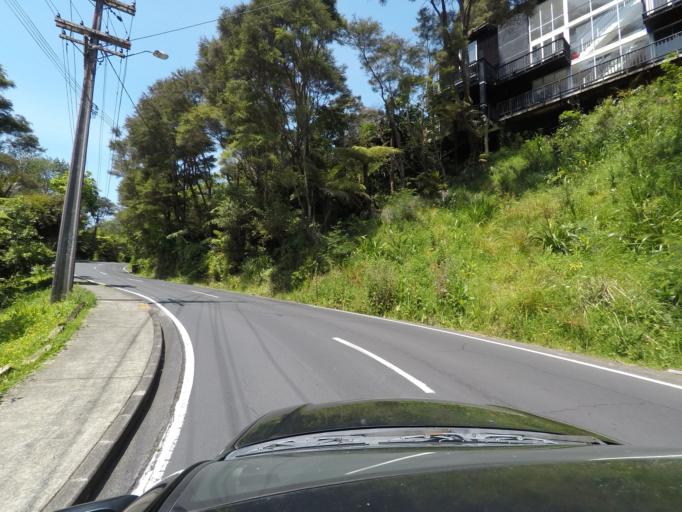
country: NZ
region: Auckland
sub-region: Auckland
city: Titirangi
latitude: -36.9613
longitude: 174.6396
